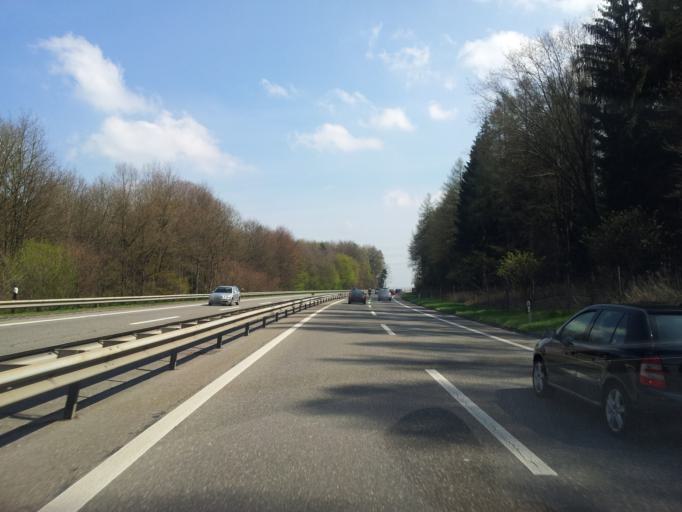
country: CH
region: Aargau
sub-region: Bezirk Brugg
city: Rupperswil
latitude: 47.3908
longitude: 8.1124
